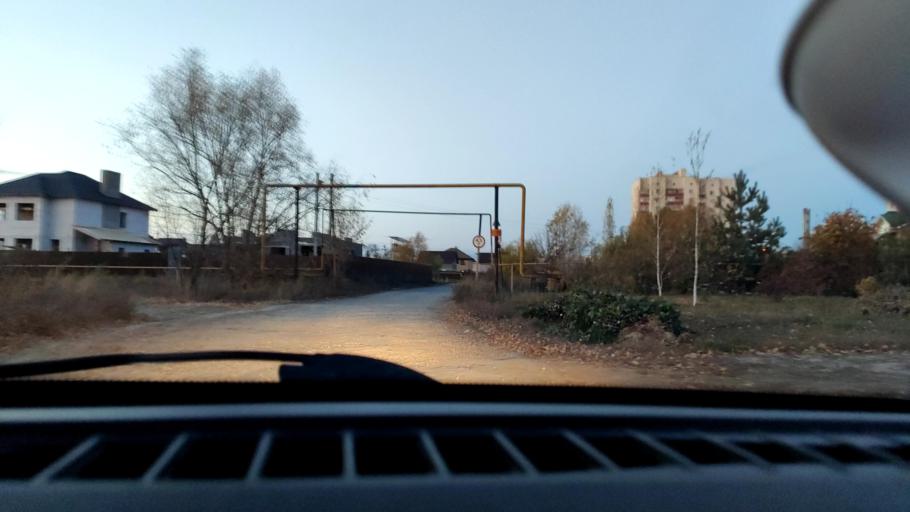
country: RU
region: Samara
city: Samara
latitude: 53.1477
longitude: 50.0879
